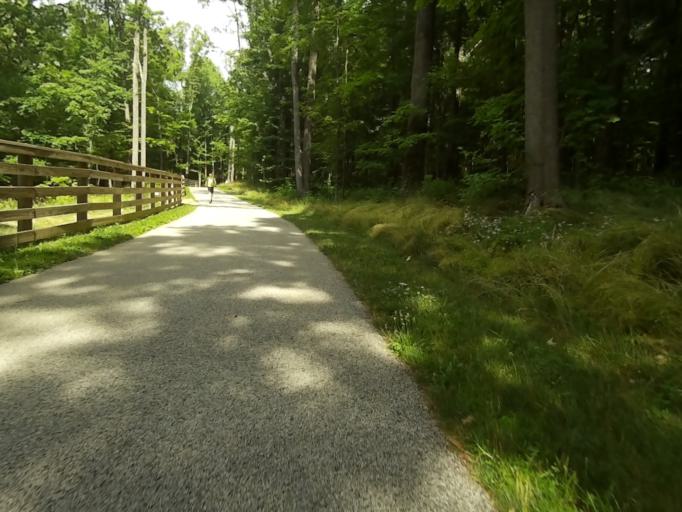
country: US
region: Ohio
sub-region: Summit County
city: Boston Heights
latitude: 41.2782
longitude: -81.5400
